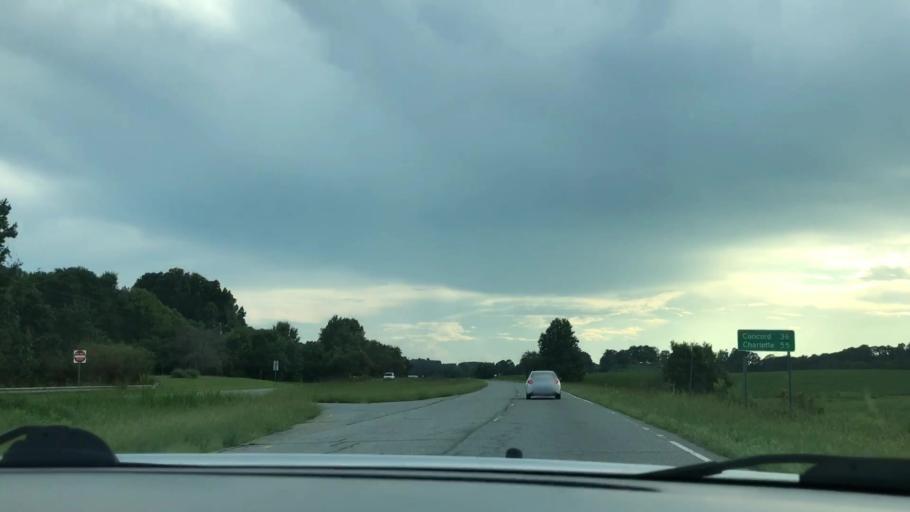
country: US
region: North Carolina
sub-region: Davidson County
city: Denton
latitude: 35.5979
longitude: -80.0358
